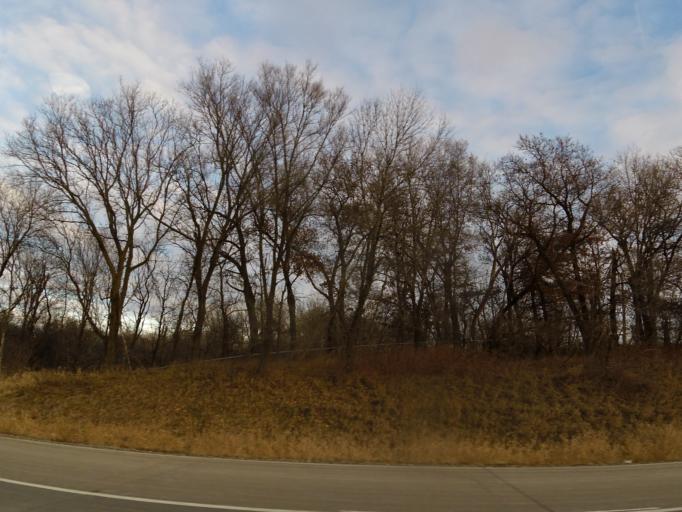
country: US
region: Minnesota
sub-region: Ramsey County
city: Vadnais Heights
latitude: 45.0614
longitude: -93.0565
